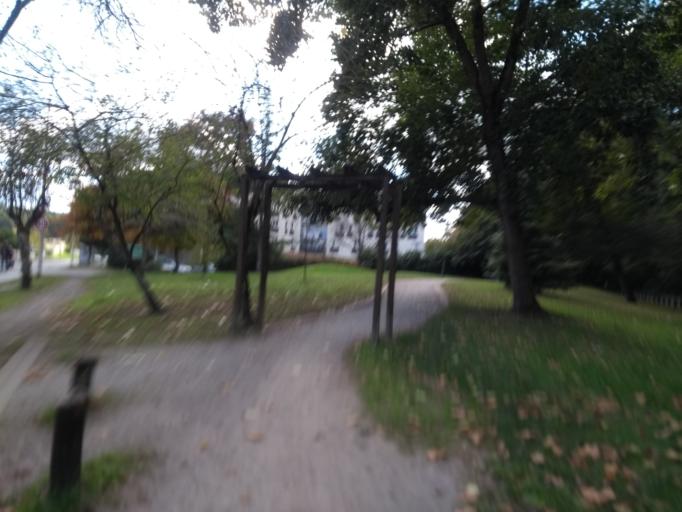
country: FR
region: Aquitaine
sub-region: Departement de la Gironde
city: Gradignan
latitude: 44.7710
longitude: -0.6006
